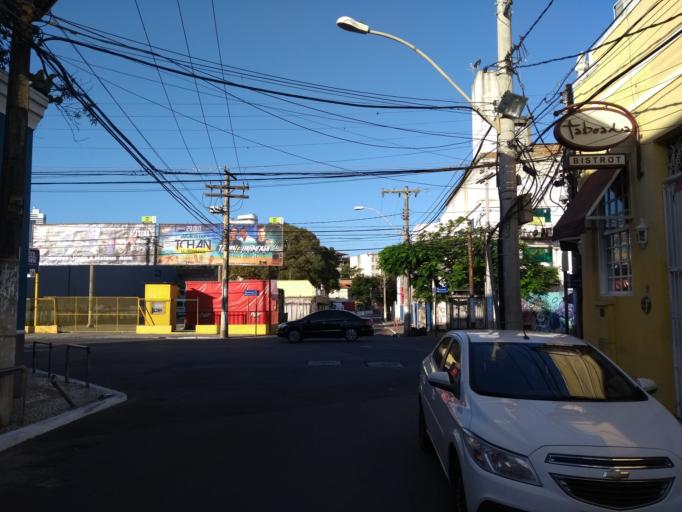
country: BR
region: Bahia
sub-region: Salvador
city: Salvador
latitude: -13.0109
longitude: -38.4914
